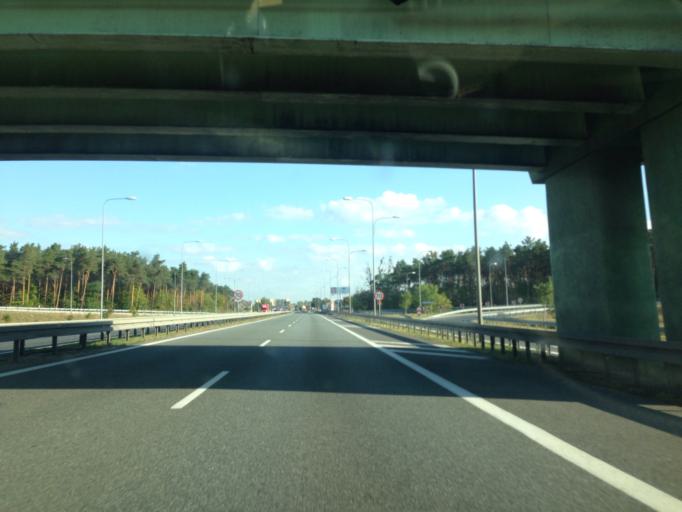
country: PL
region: Kujawsko-Pomorskie
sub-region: Bydgoszcz
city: Bydgoszcz
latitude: 53.0923
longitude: 18.0081
